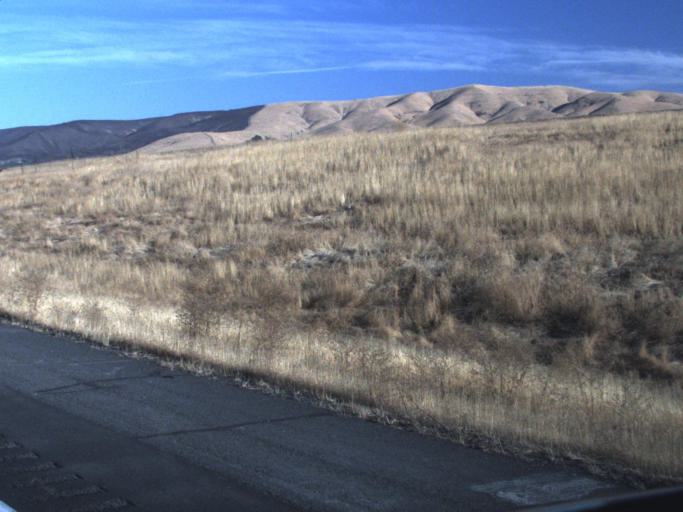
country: US
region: Washington
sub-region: Yakima County
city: Wapato
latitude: 46.4725
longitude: -120.3979
